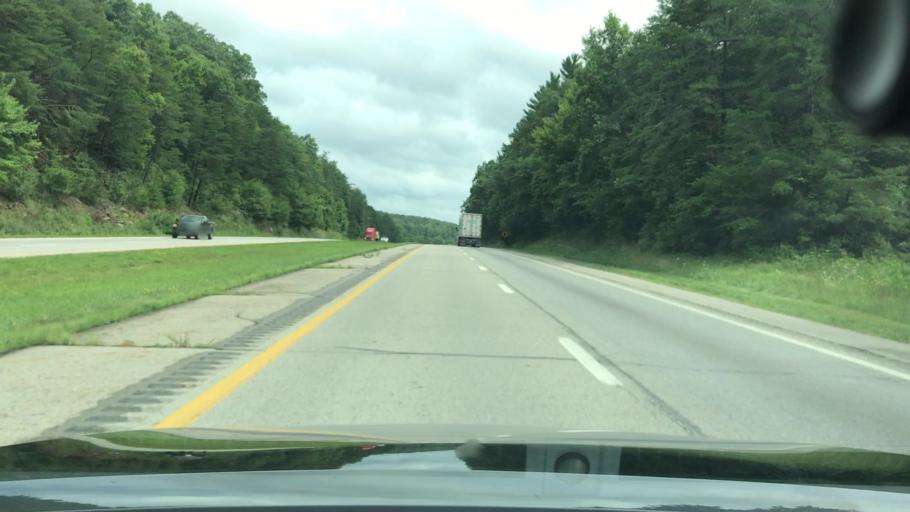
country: US
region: Ohio
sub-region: Jackson County
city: Jackson
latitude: 39.1185
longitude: -82.6872
